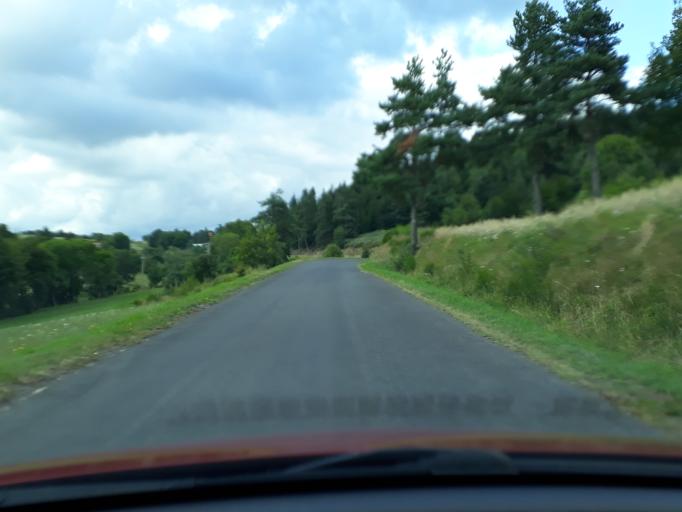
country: FR
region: Auvergne
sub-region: Departement de la Haute-Loire
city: Le Monastier-sur-Gazeille
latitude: 44.8338
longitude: 3.9449
